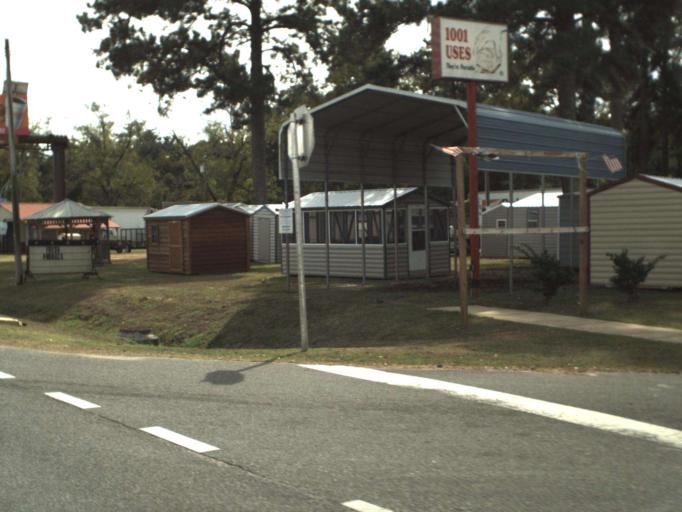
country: US
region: Florida
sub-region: Leon County
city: Tallahassee
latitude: 30.5000
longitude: -84.3281
